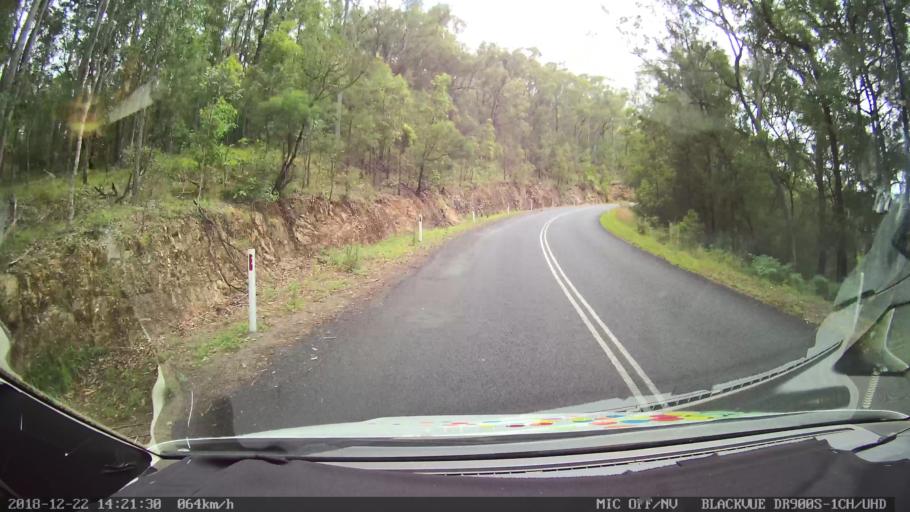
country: AU
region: New South Wales
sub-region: Clarence Valley
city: Coutts Crossing
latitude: -30.0210
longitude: 152.6581
